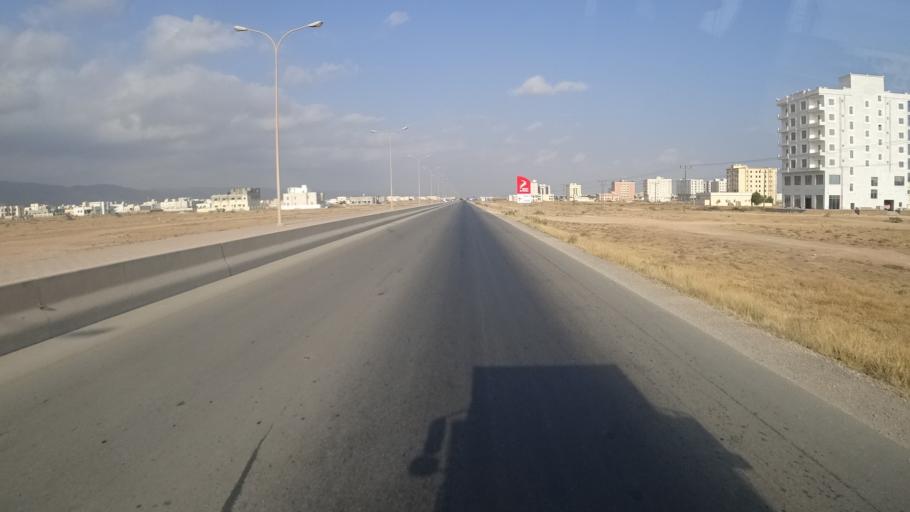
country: OM
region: Zufar
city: Salalah
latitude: 17.0258
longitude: 54.0216
